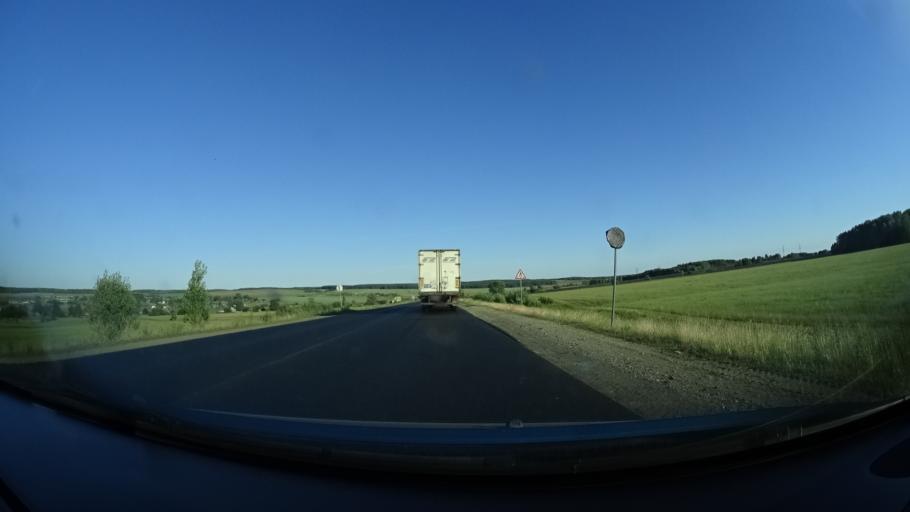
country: RU
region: Sverdlovsk
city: Achit
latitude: 56.8980
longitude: 57.6010
